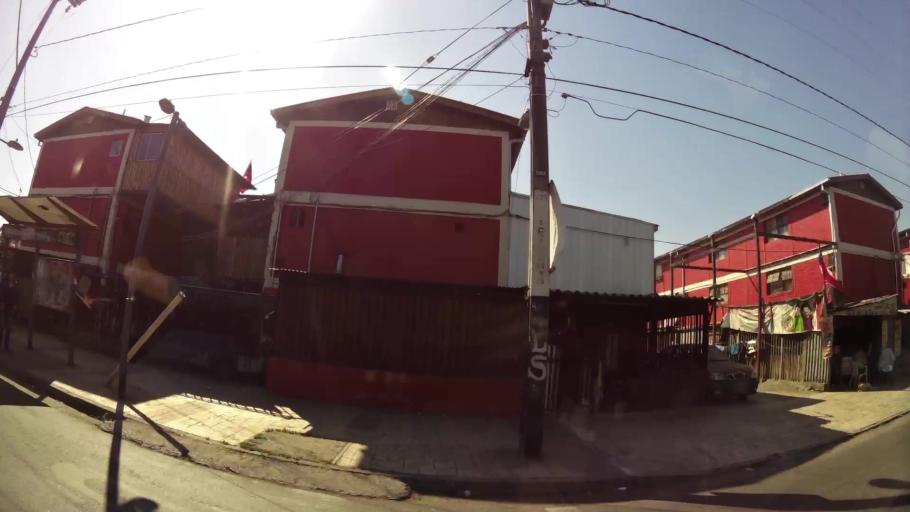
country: CL
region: Santiago Metropolitan
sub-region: Provincia de Santiago
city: La Pintana
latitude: -33.5590
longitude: -70.6271
